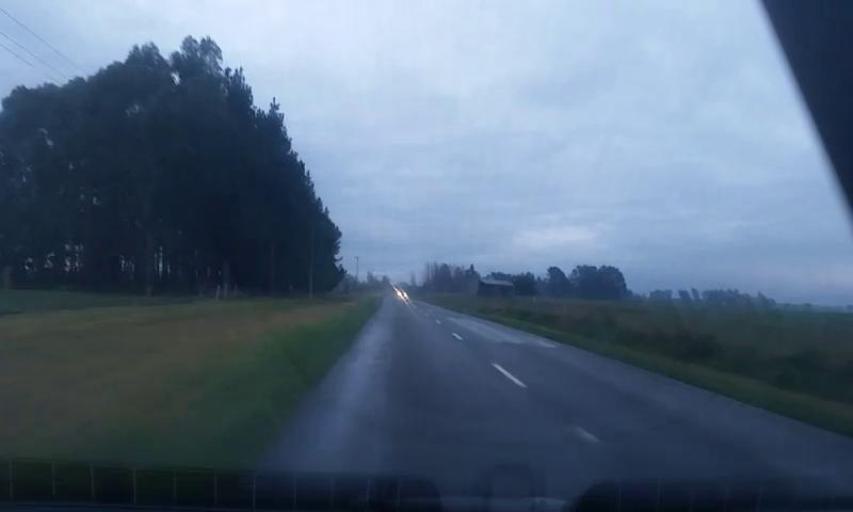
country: NZ
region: Canterbury
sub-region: Ashburton District
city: Rakaia
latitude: -43.7585
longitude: 171.9673
